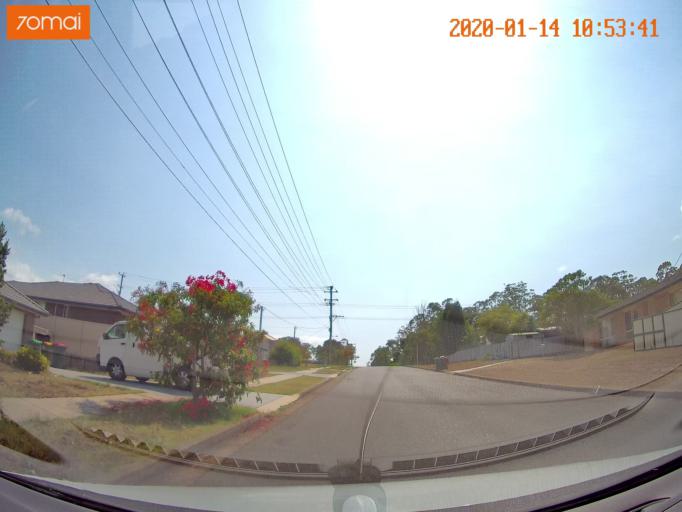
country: AU
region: New South Wales
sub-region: Lake Macquarie Shire
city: Dora Creek
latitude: -33.1012
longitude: 151.4876
